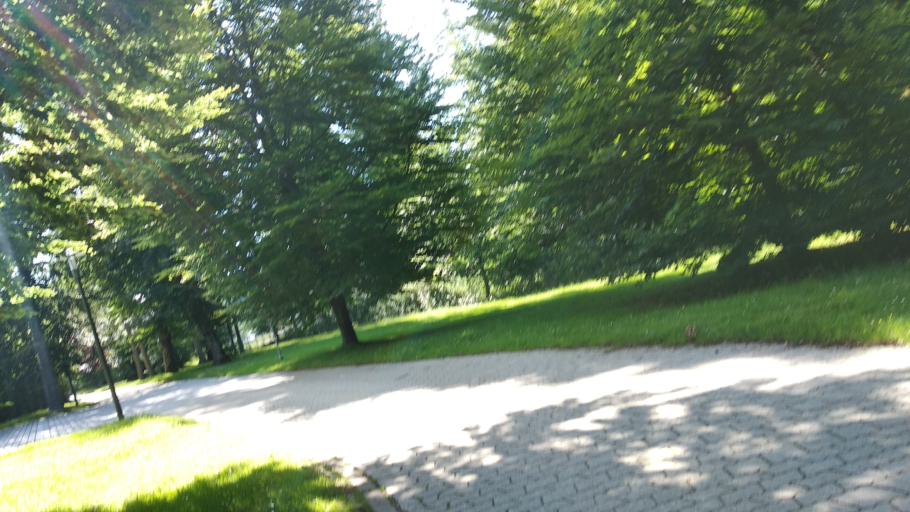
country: DE
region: Bavaria
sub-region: Upper Bavaria
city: Kirchseeon
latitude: 48.0651
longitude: 11.8967
